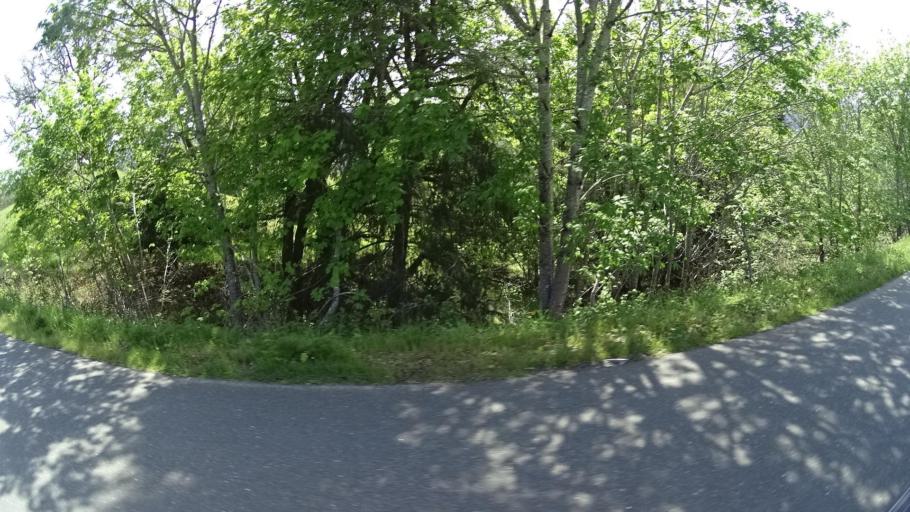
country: US
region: California
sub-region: Humboldt County
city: Redway
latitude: 40.4133
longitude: -123.7579
